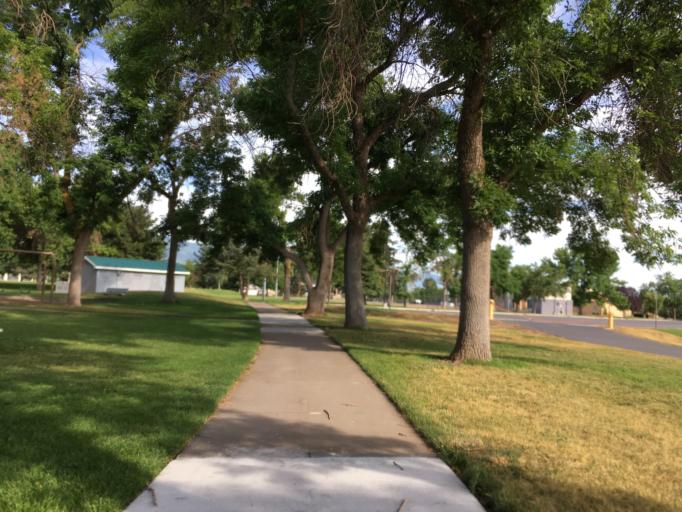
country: US
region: Utah
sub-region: Davis County
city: Hill Air Force Bace
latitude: 41.0840
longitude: -111.9979
